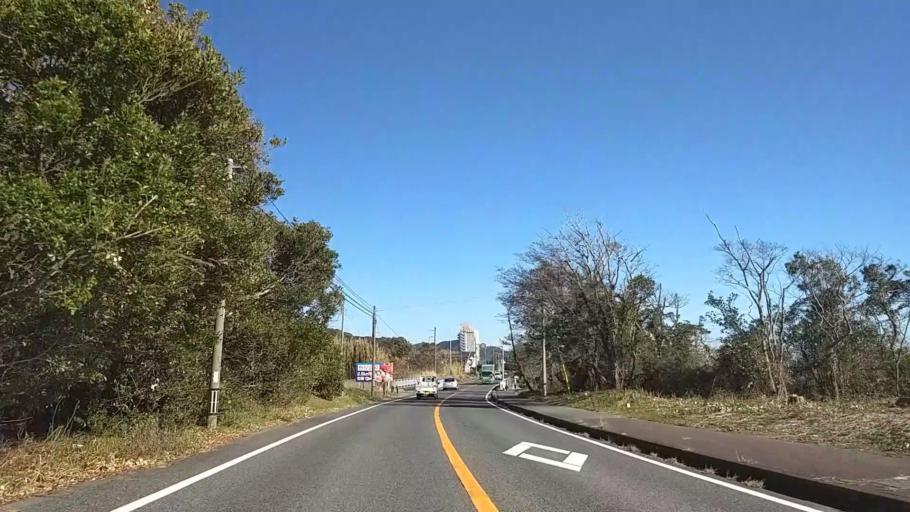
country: JP
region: Chiba
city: Kawaguchi
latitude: 35.0471
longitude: 140.0265
